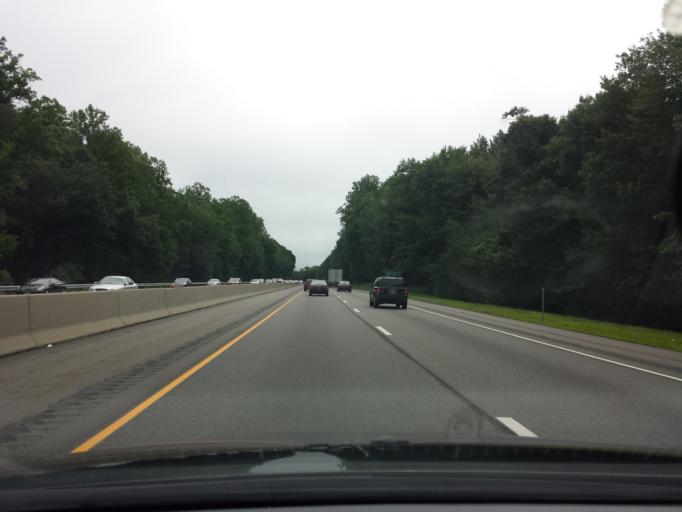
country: US
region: Connecticut
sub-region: Middlesex County
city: Westbrook Center
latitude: 41.2928
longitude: -72.4766
